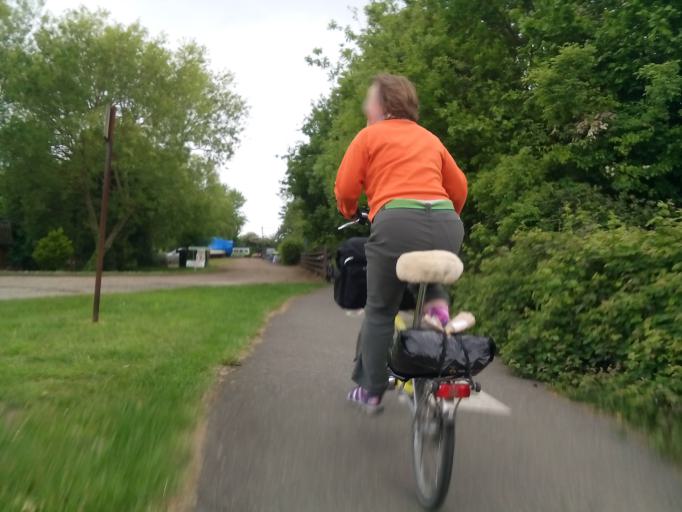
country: GB
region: England
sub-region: Cambridgeshire
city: Godmanchester
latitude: 52.3376
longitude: -0.1439
